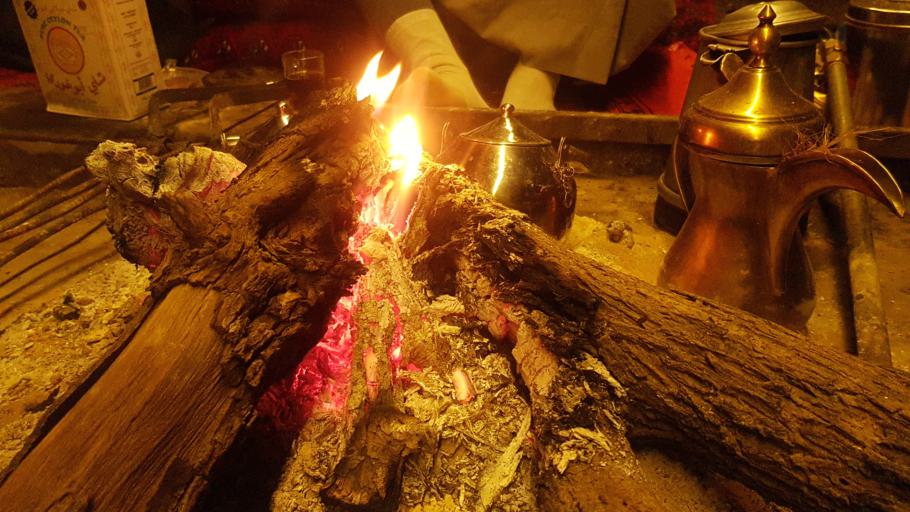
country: SA
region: Al-Qassim
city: Buraydah
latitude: 26.5941
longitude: 44.0611
